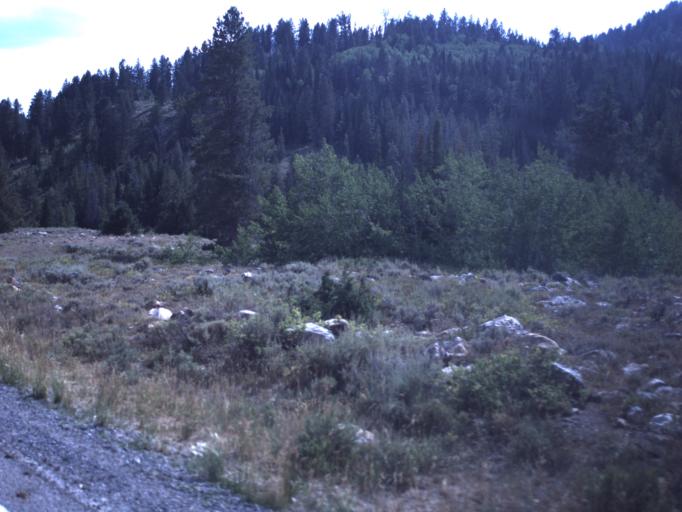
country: US
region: Utah
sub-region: Cache County
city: Richmond
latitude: 41.9695
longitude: -111.5320
